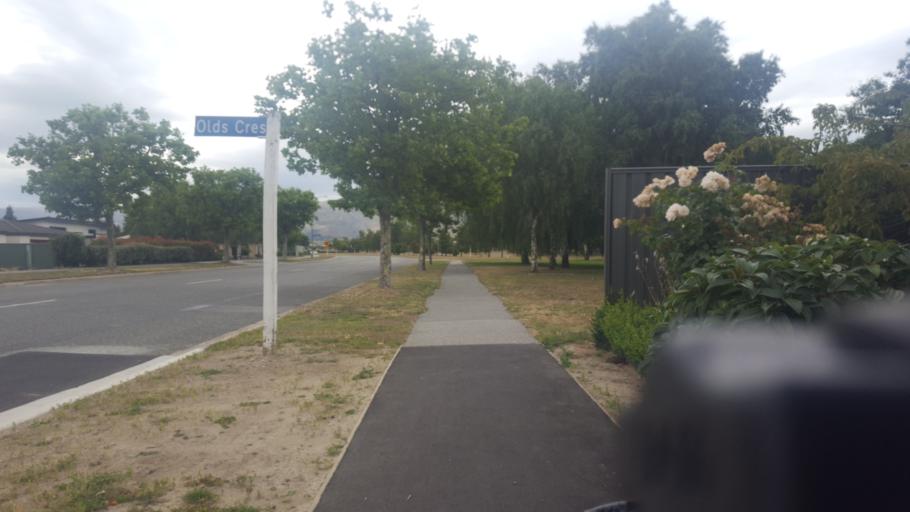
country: NZ
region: Otago
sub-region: Queenstown-Lakes District
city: Wanaka
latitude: -45.0470
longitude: 169.1861
